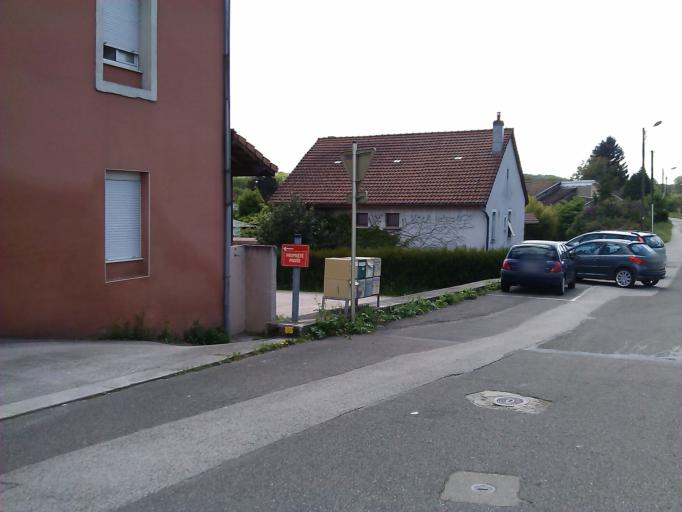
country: FR
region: Franche-Comte
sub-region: Departement du Doubs
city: Voujeaucourt
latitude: 47.4796
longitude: 6.7662
